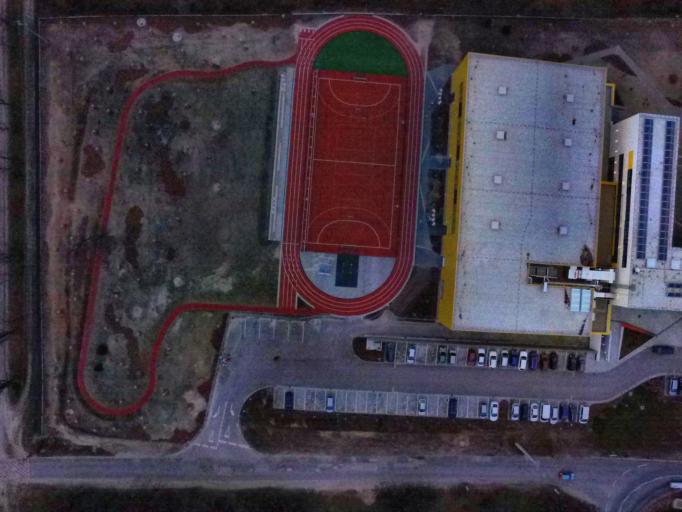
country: HU
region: Pest
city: Dunakeszi
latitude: 47.6189
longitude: 19.1535
